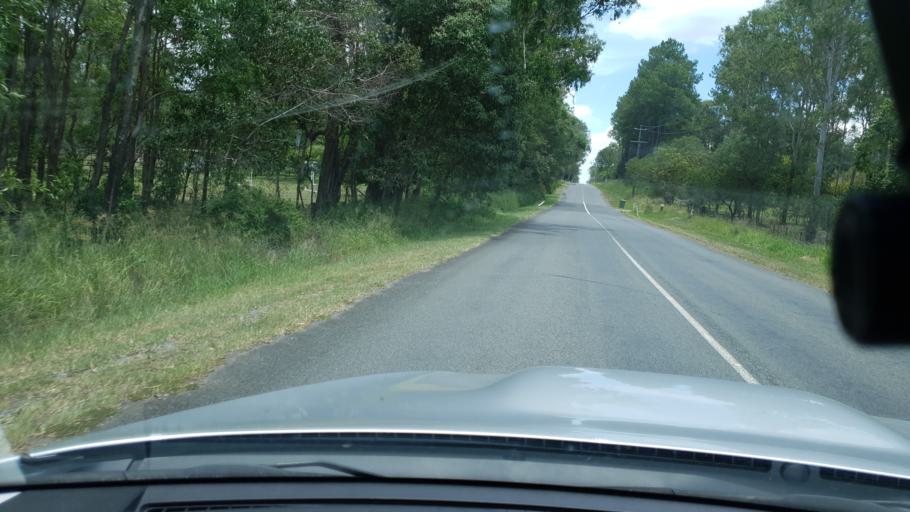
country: AU
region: Queensland
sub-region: Logan
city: North Maclean
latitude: -27.7728
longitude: 152.9951
